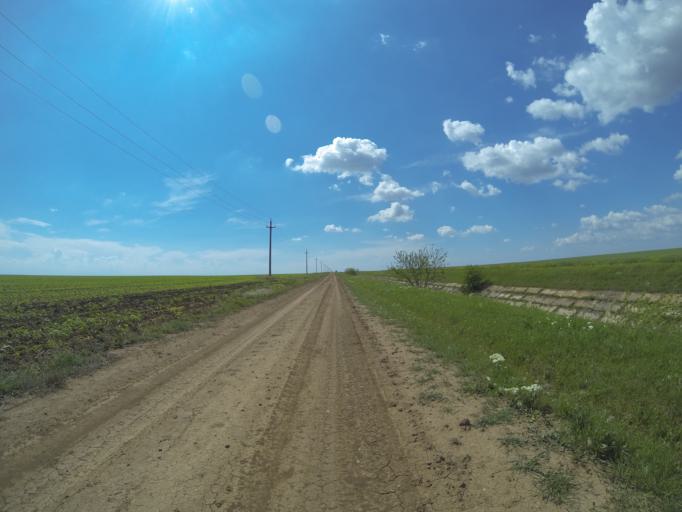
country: RO
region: Dolj
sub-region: Comuna Dranicu
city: Dranic
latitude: 44.0164
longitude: 23.7884
